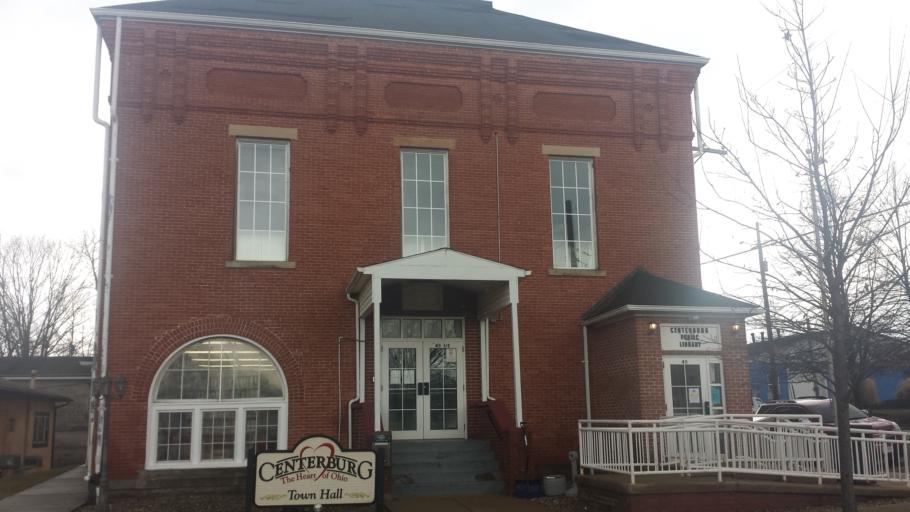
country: US
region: Ohio
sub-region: Knox County
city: Centerburg
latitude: 40.3051
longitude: -82.6951
